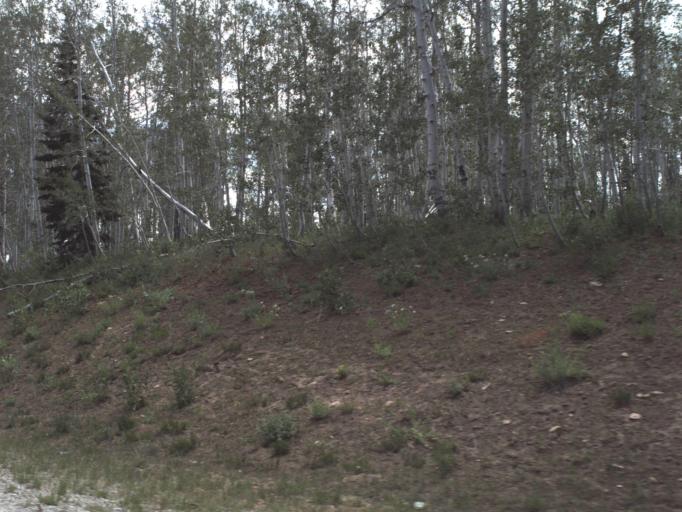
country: US
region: Utah
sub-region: Rich County
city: Randolph
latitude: 41.4746
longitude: -111.4824
